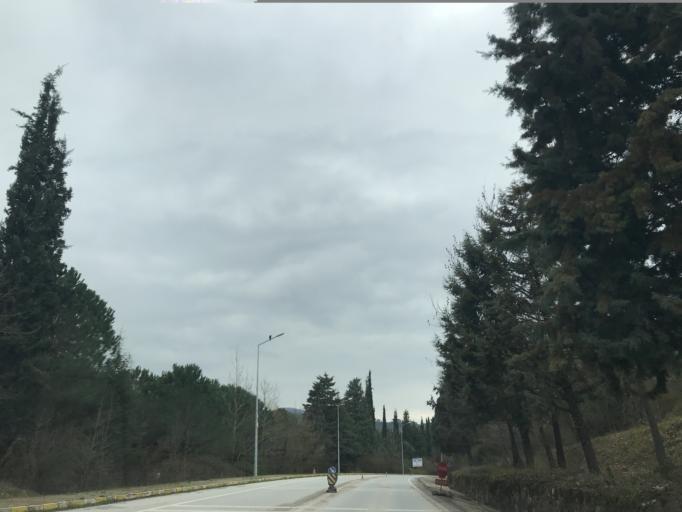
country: TR
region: Yalova
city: Termal
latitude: 40.6044
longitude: 29.1880
